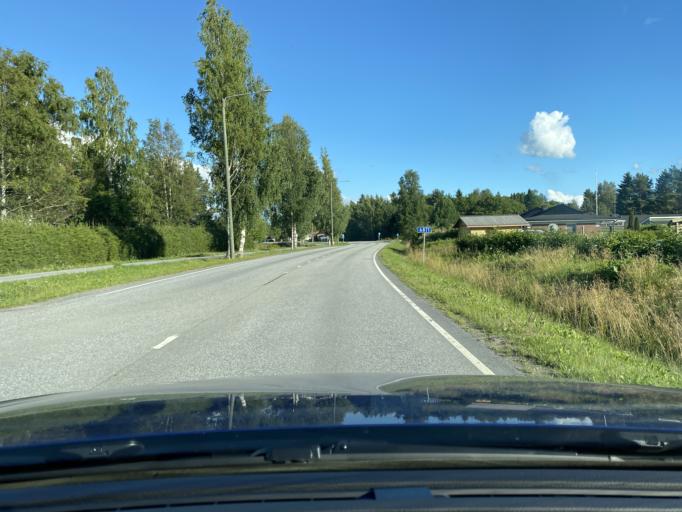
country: FI
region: Ostrobothnia
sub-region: Kyroenmaa
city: Laihia
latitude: 62.9775
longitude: 22.0022
